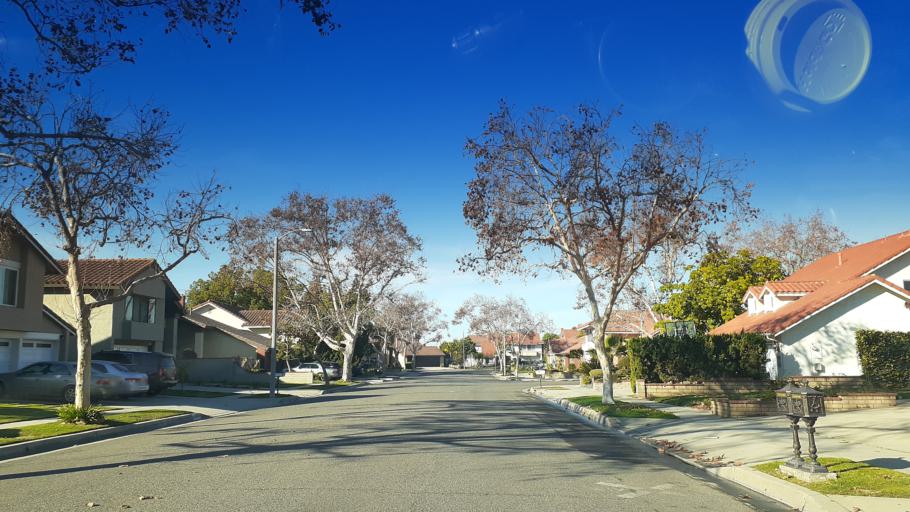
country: US
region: California
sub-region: Los Angeles County
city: Cerritos
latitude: 33.8467
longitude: -118.0649
